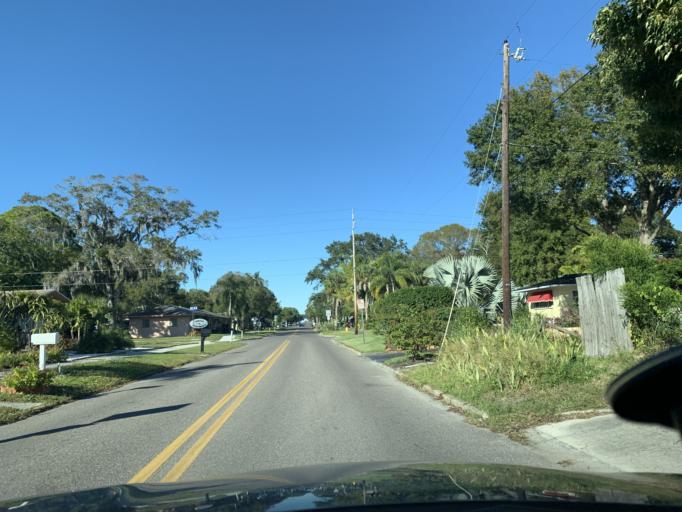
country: US
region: Florida
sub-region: Pinellas County
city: Gulfport
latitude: 27.7406
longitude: -82.6997
